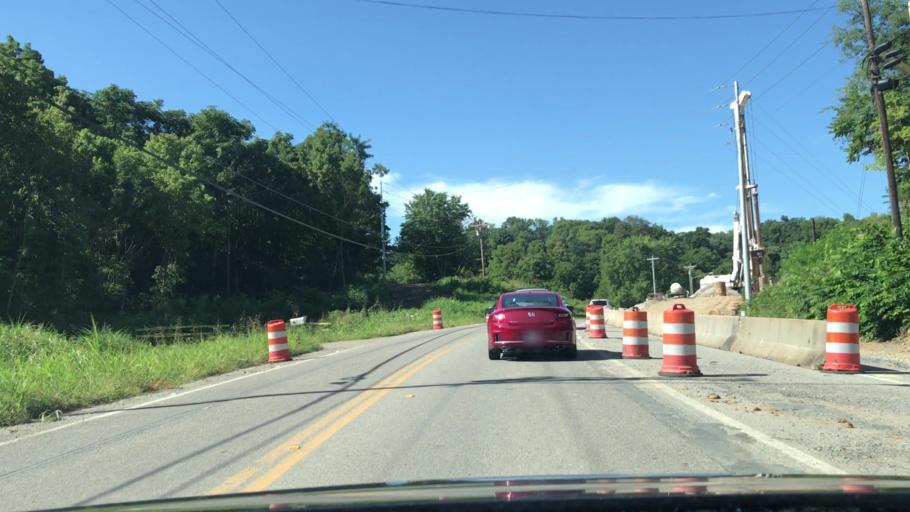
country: US
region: Tennessee
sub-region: Williamson County
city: Brentwood Estates
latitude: 35.9785
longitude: -86.8234
